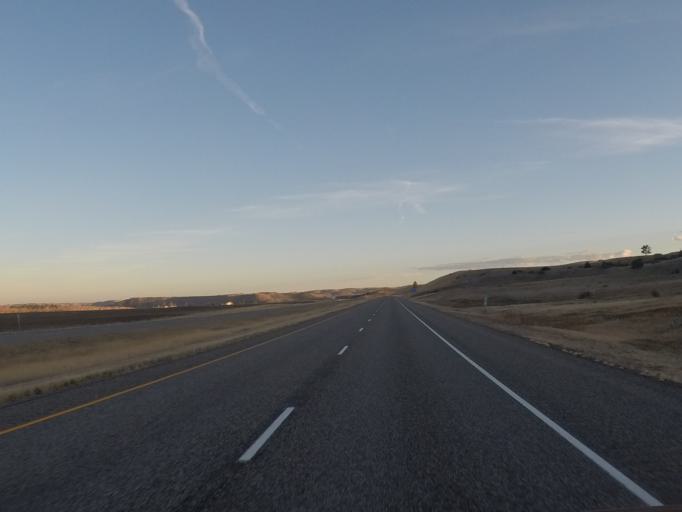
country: US
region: Montana
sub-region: Sweet Grass County
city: Big Timber
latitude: 45.7576
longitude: -109.7837
